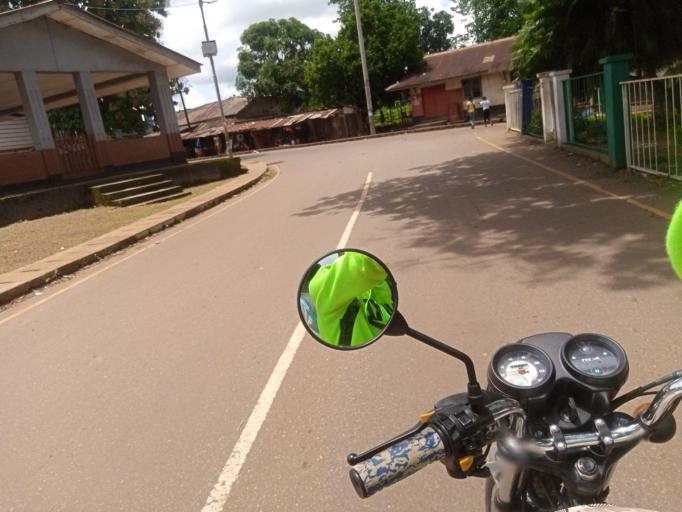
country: SL
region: Northern Province
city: Port Loko
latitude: 8.7651
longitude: -12.7889
